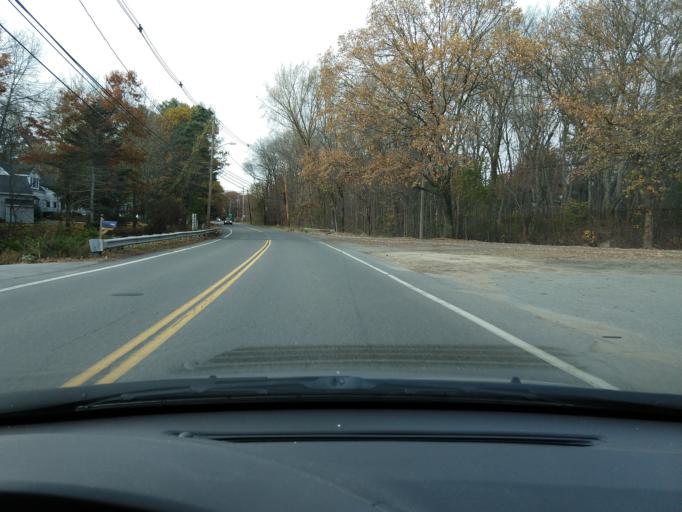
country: US
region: Massachusetts
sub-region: Middlesex County
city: Bedford
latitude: 42.5187
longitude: -71.2859
